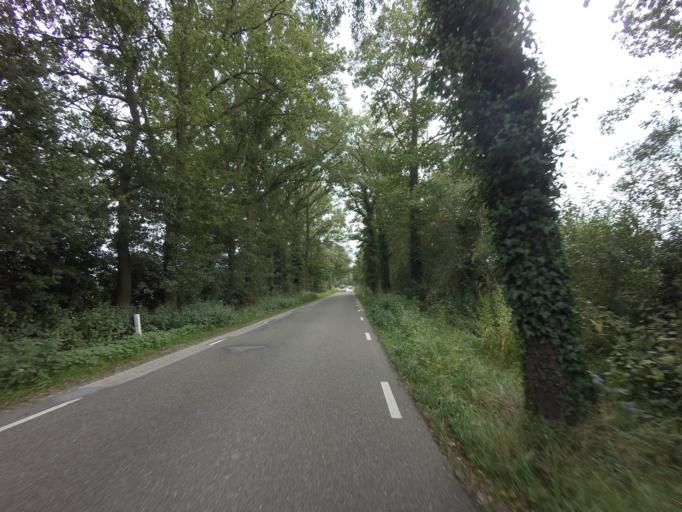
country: NL
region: Overijssel
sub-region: Gemeente Enschede
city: Enschede
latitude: 52.1859
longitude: 6.9392
